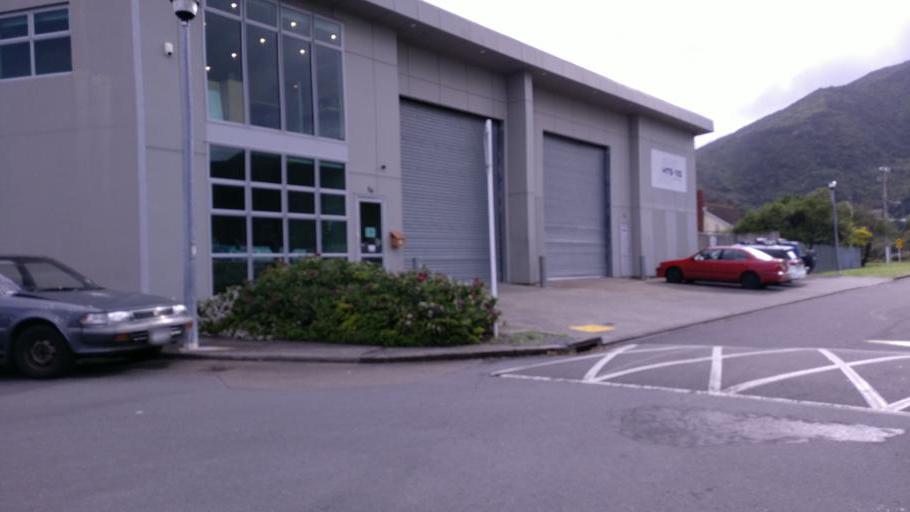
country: NZ
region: Wellington
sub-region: Lower Hutt City
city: Lower Hutt
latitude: -41.2334
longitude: 174.9133
